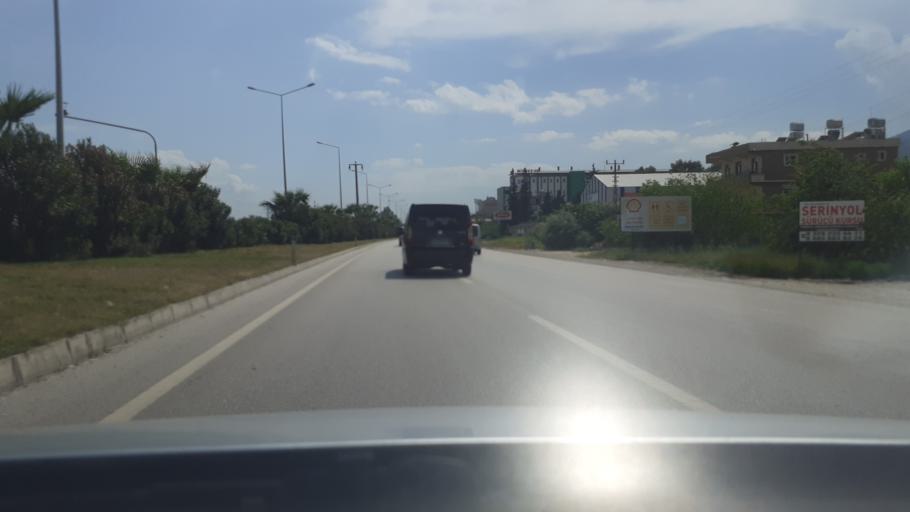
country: TR
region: Hatay
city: Serinyol
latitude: 36.3573
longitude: 36.2185
